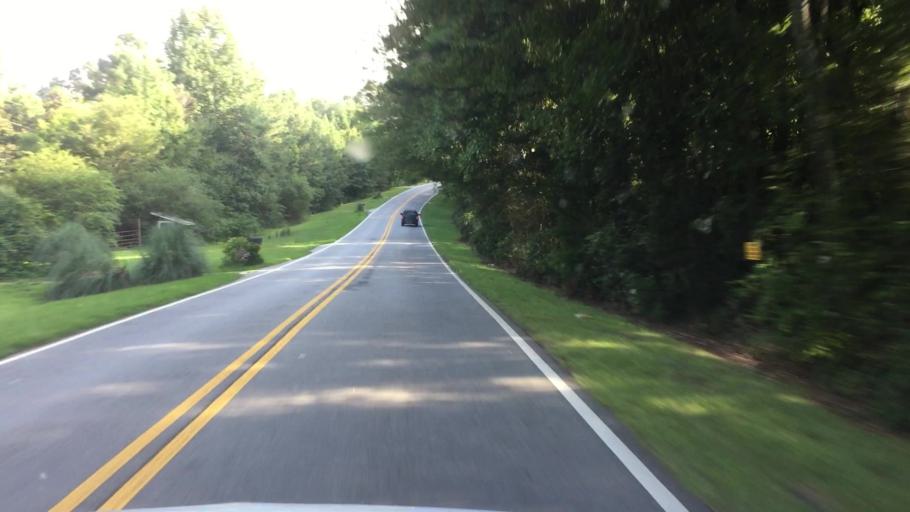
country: US
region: Georgia
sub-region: DeKalb County
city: Pine Mountain
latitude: 33.6201
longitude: -84.1316
